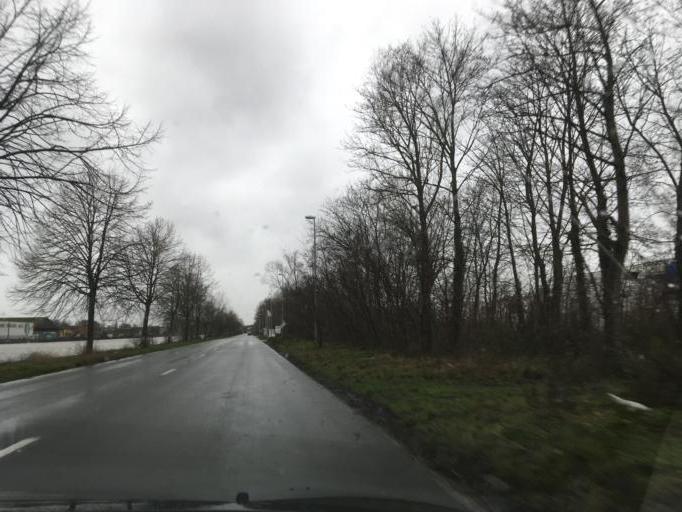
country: BE
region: Flanders
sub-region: Provincie West-Vlaanderen
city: Izegem
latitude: 50.9244
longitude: 3.2101
